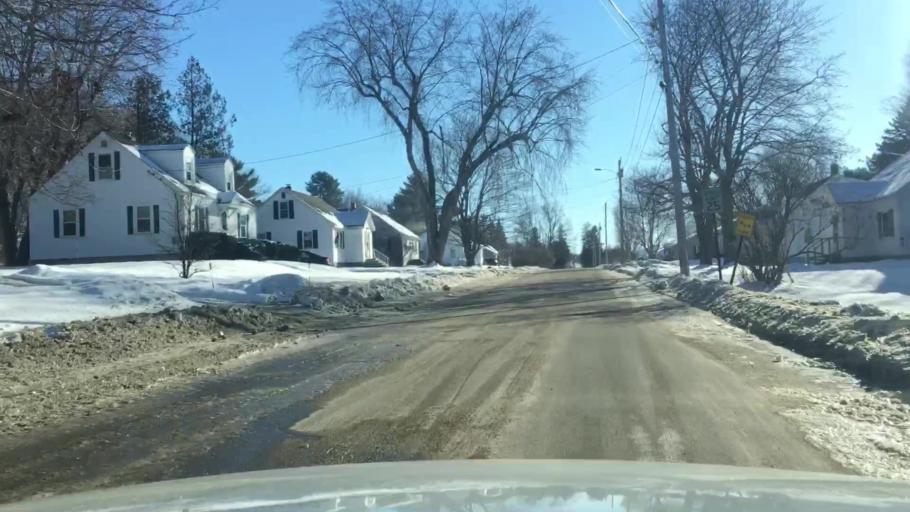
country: US
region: Maine
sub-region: Kennebec County
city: Winthrop
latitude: 44.3111
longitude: -69.9695
